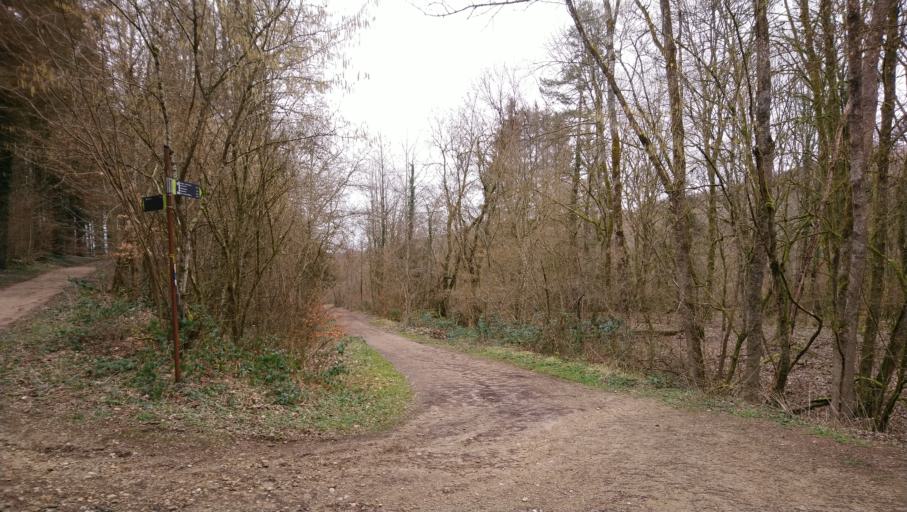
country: FR
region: Lorraine
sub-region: Departement de la Moselle
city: Audun-le-Tiche
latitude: 49.4663
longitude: 5.9759
